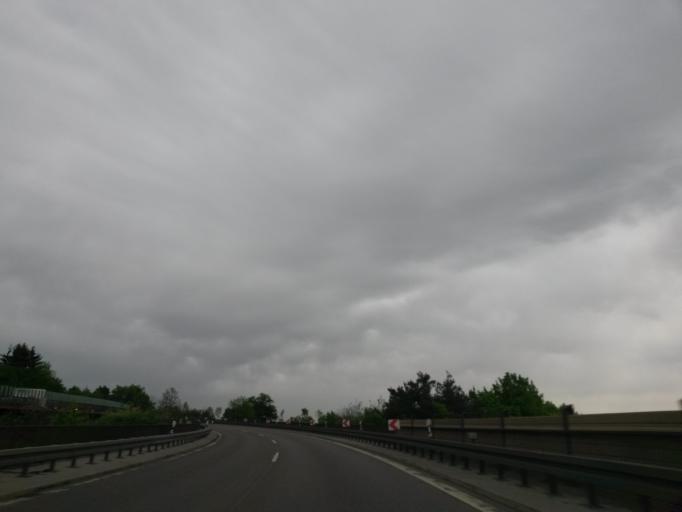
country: DE
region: Baden-Wuerttemberg
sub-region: Regierungsbezirk Stuttgart
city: Kornwestheim
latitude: 48.8394
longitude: 9.1703
